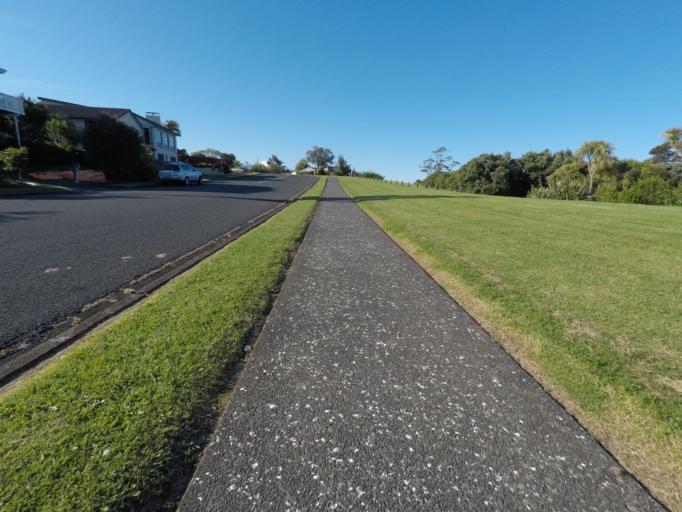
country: NZ
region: Auckland
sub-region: Auckland
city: Rosebank
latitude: -36.8336
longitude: 174.6606
